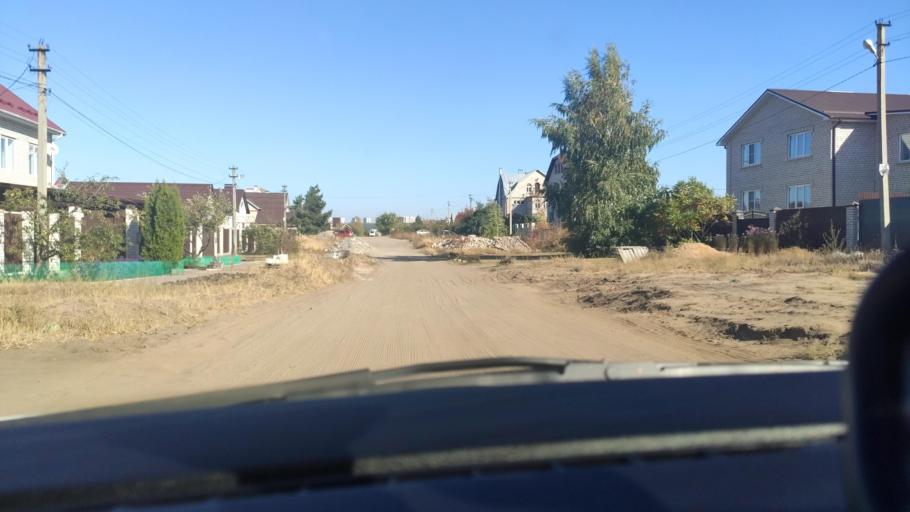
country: RU
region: Voronezj
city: Pridonskoy
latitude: 51.6290
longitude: 39.0946
